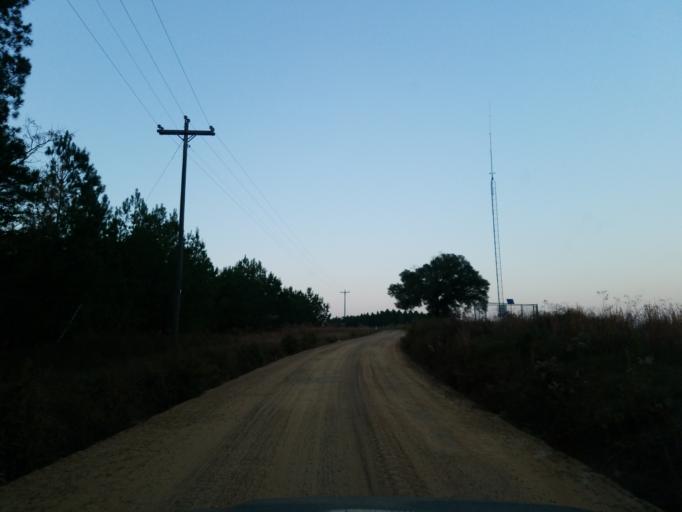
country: US
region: Georgia
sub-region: Turner County
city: Ashburn
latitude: 31.7241
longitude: -83.4815
